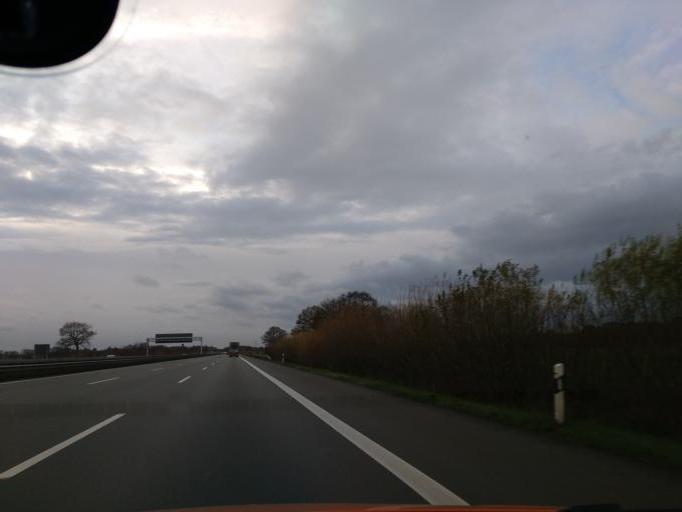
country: DE
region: Lower Saxony
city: Halvesbostel
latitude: 53.3349
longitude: 9.6246
